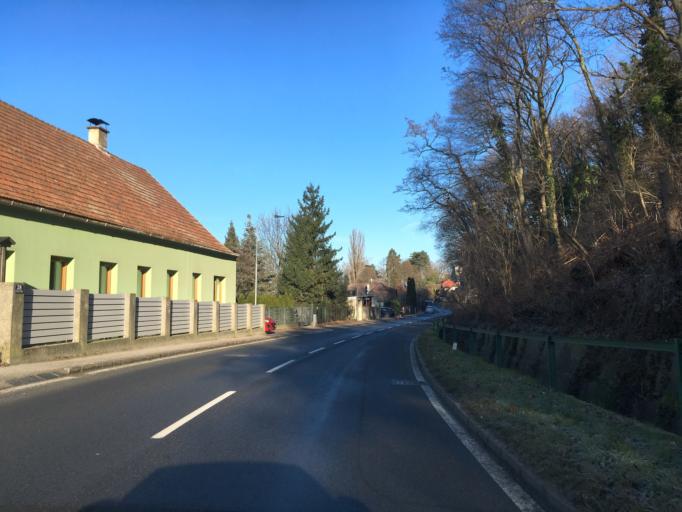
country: AT
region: Lower Austria
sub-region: Politischer Bezirk Tulln
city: Wordern
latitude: 48.3369
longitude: 16.2294
